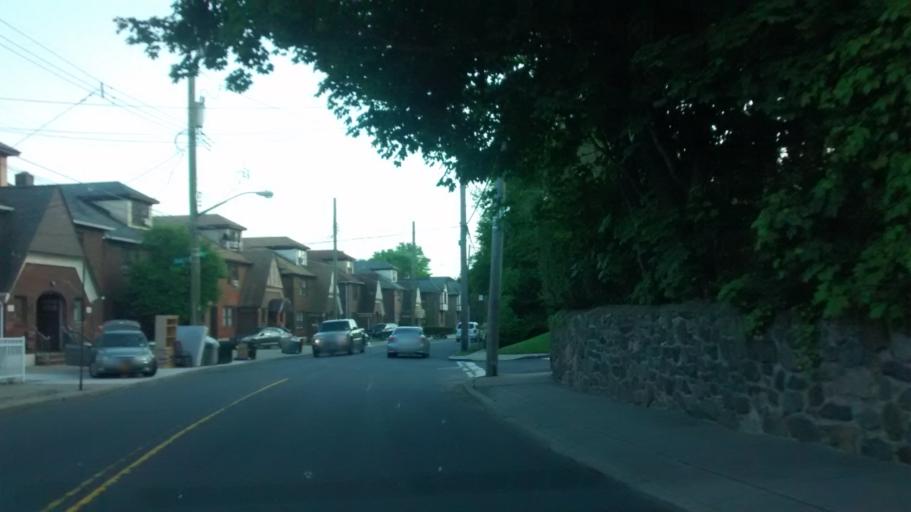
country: US
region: New York
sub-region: Richmond County
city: Staten Island
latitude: 40.5719
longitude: -74.1215
